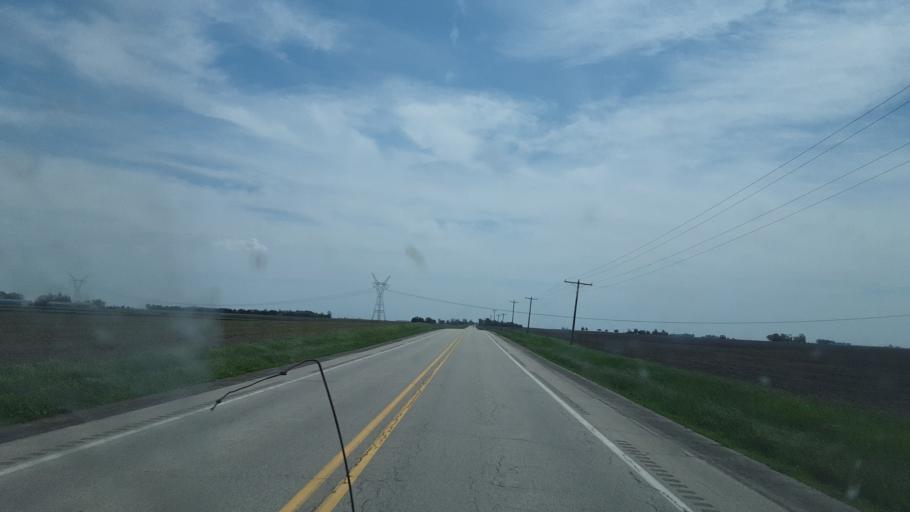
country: US
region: Illinois
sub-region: McLean County
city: Heyworth
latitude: 40.3123
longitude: -88.9390
